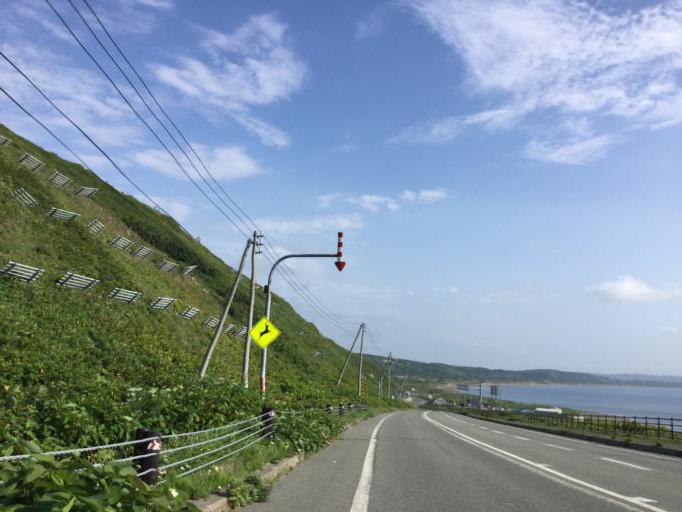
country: JP
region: Hokkaido
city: Wakkanai
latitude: 45.3784
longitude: 141.6541
